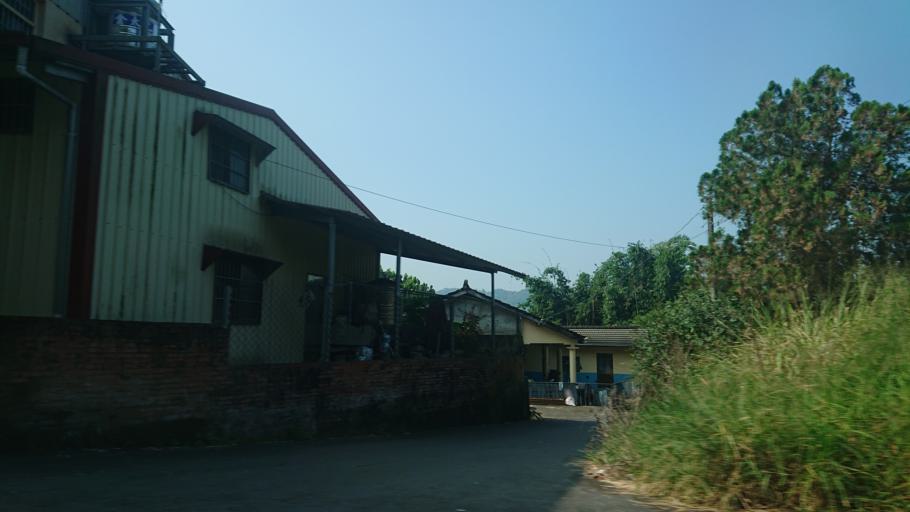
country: TW
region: Taiwan
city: Lugu
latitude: 23.6956
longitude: 120.6628
